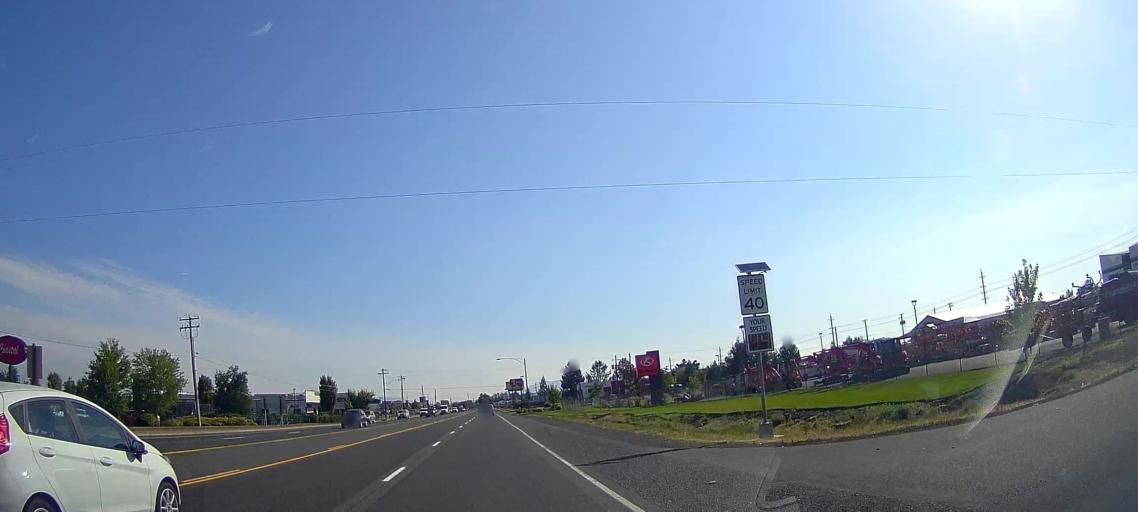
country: US
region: Oregon
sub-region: Deschutes County
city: Redmond
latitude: 44.2463
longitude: -121.1892
